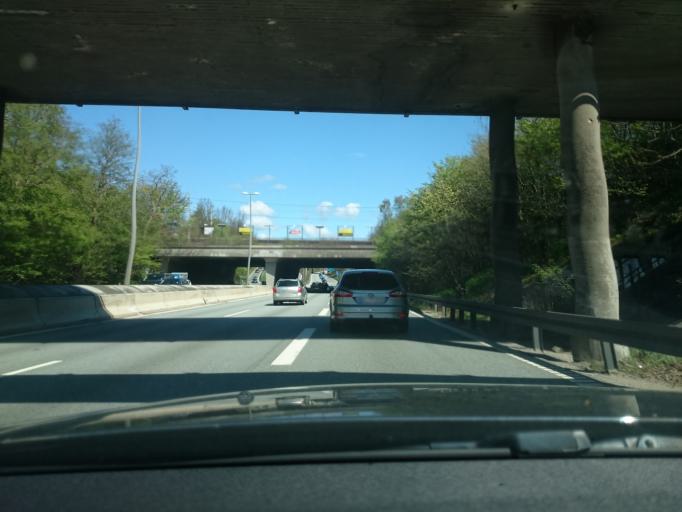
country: DK
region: Capital Region
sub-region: Lyngby-Tarbaek Kommune
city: Kongens Lyngby
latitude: 55.7613
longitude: 12.5195
